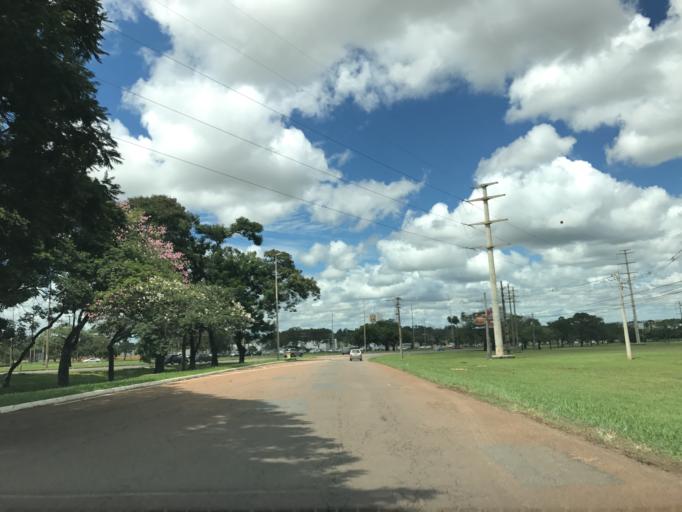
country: BR
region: Federal District
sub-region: Brasilia
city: Brasilia
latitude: -15.8112
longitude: -47.9495
